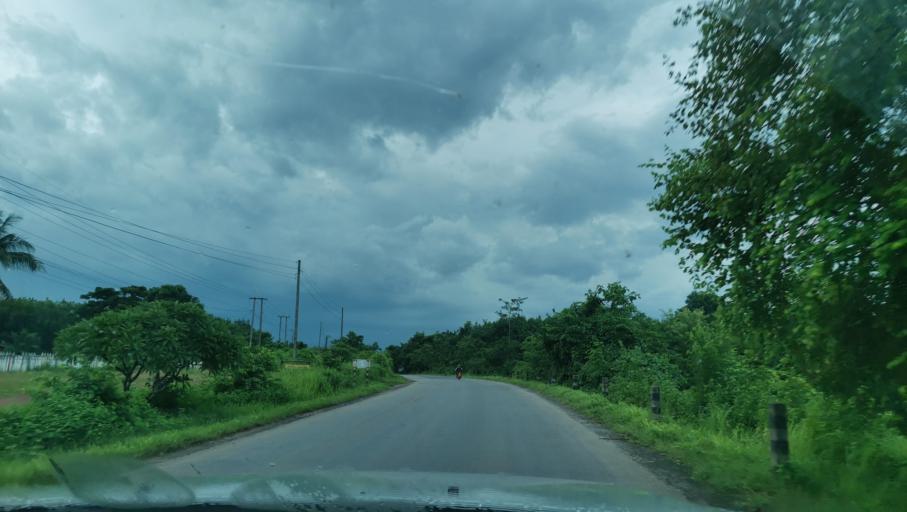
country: TH
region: Nakhon Phanom
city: Ban Phaeng
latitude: 17.8538
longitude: 104.4318
